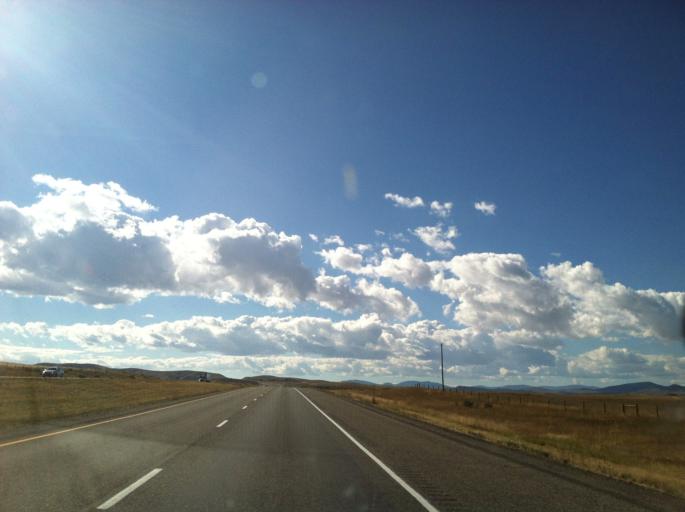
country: US
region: Montana
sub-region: Gallatin County
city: Three Forks
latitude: 45.9191
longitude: -111.6258
